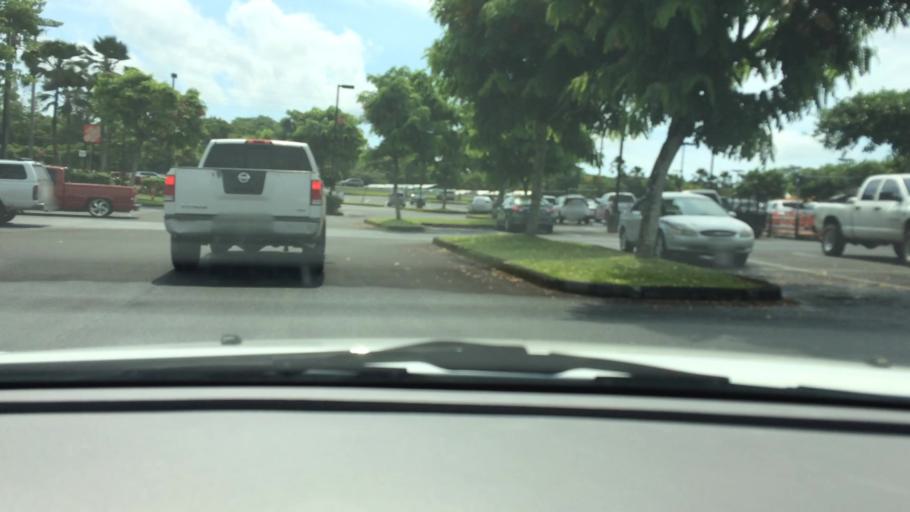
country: US
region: Hawaii
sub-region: Hawaii County
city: Hilo
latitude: 19.6990
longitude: -155.0597
